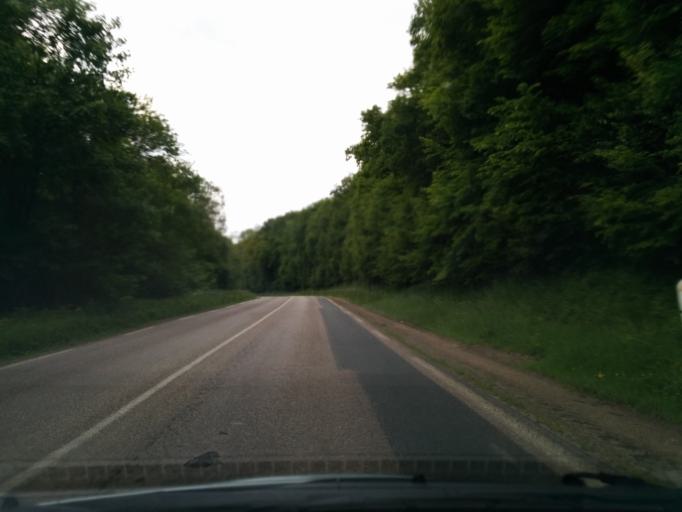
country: FR
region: Haute-Normandie
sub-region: Departement de l'Eure
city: Vernon
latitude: 49.1154
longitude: 1.4944
